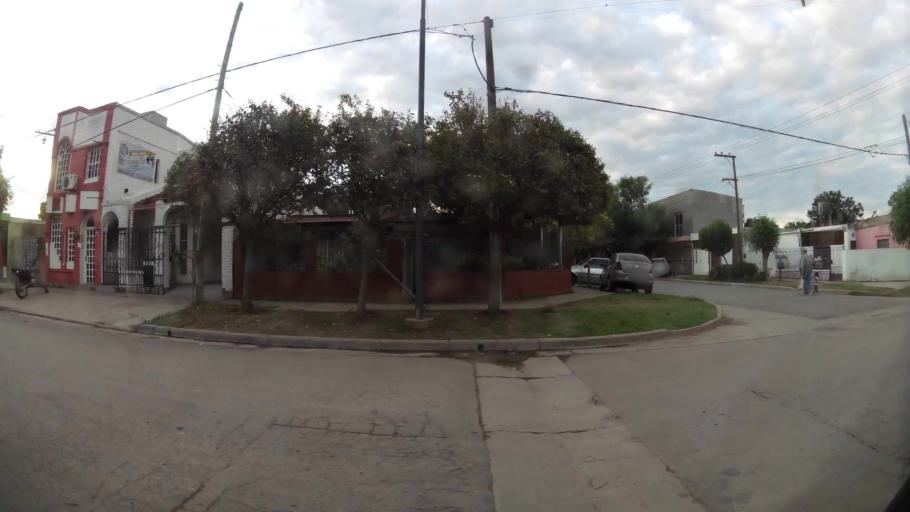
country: AR
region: Buenos Aires
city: San Nicolas de los Arroyos
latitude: -33.3186
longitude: -60.2412
